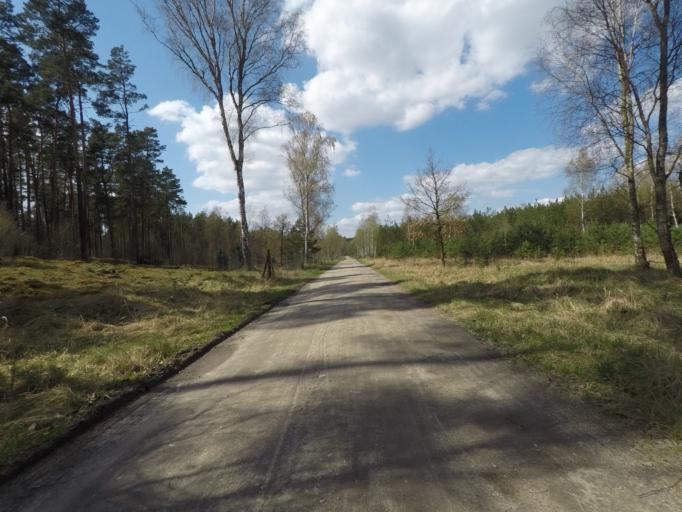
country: DE
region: Brandenburg
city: Biesenthal
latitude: 52.8278
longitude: 13.6621
